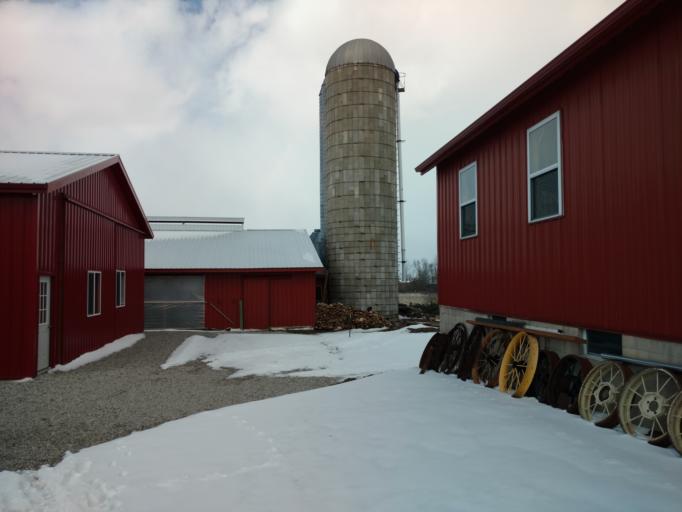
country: US
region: Michigan
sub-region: Gladwin County
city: Gladwin
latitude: 44.0358
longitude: -84.4712
